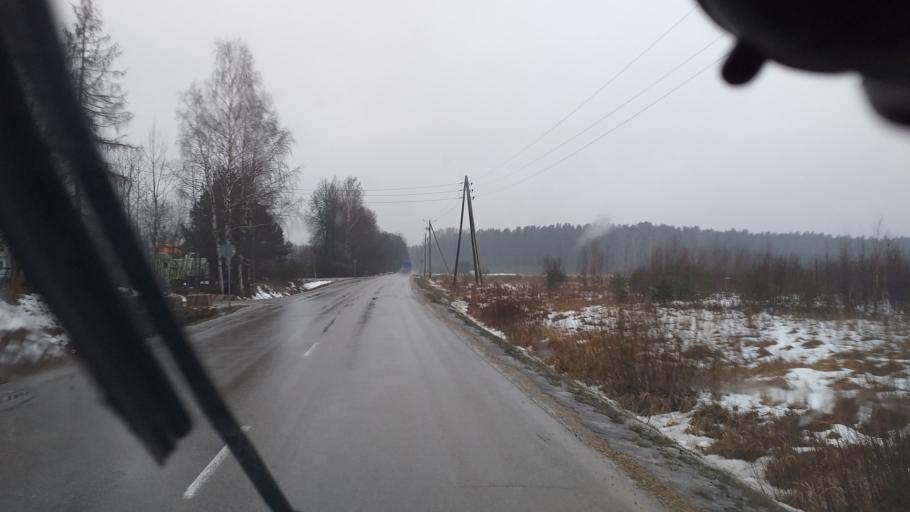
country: LV
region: Babite
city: Pinki
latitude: 56.9682
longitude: 23.9677
